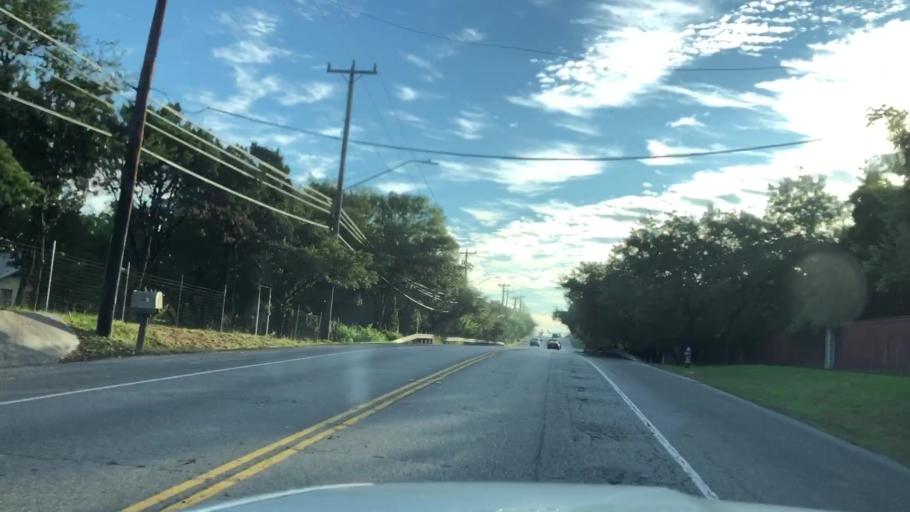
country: US
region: Texas
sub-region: Bexar County
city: Leon Valley
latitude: 29.5444
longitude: -98.6447
